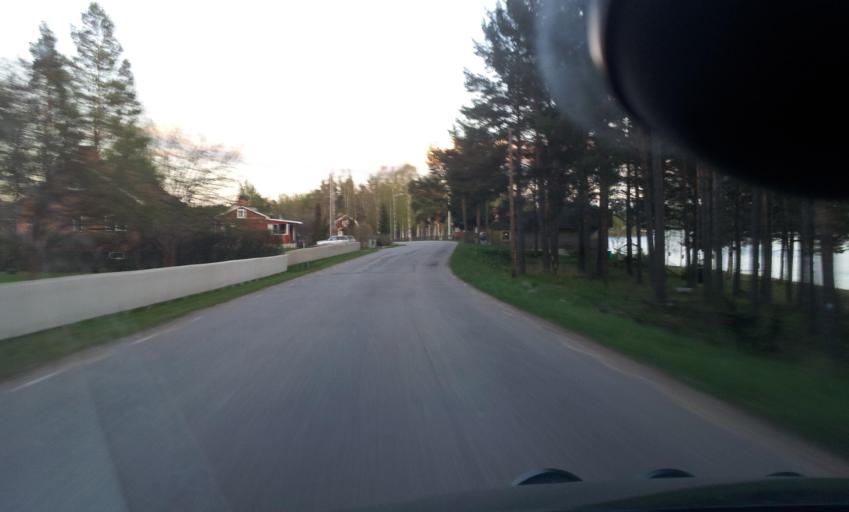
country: SE
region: Gaevleborg
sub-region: Bollnas Kommun
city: Bollnas
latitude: 61.3726
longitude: 16.3984
